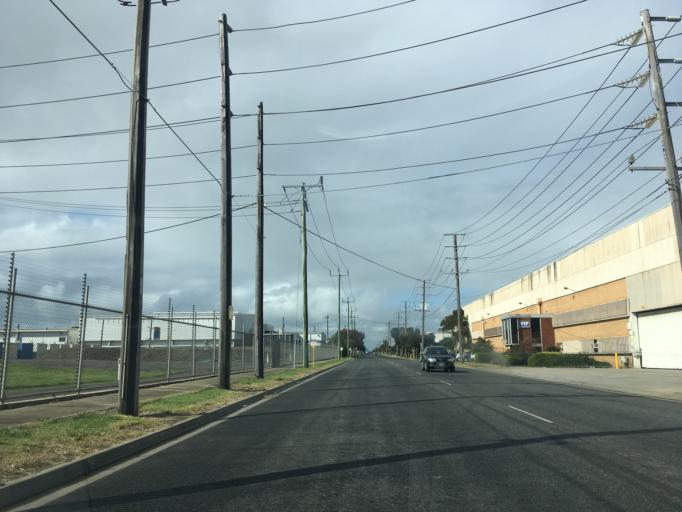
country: AU
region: Victoria
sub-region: Hobsons Bay
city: Laverton
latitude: -37.8403
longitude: 144.7898
